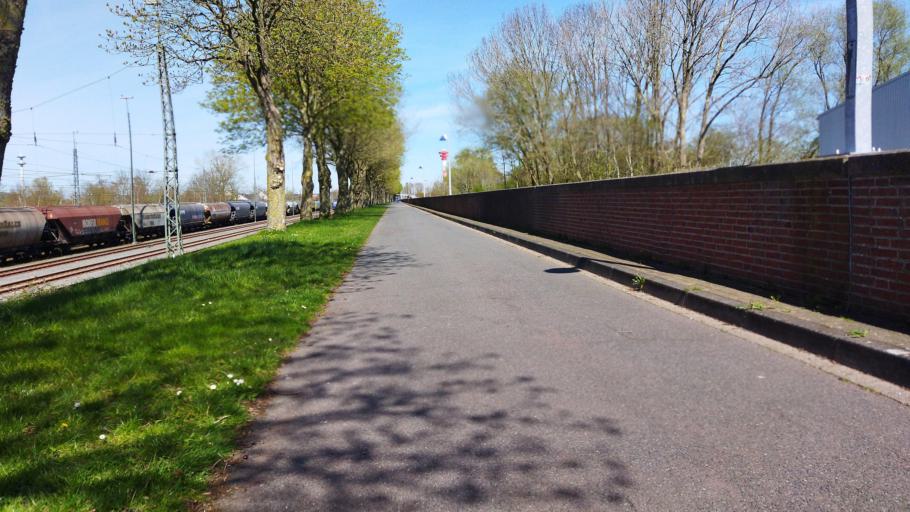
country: DE
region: Lower Saxony
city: Nordenham
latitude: 53.4768
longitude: 8.4828
